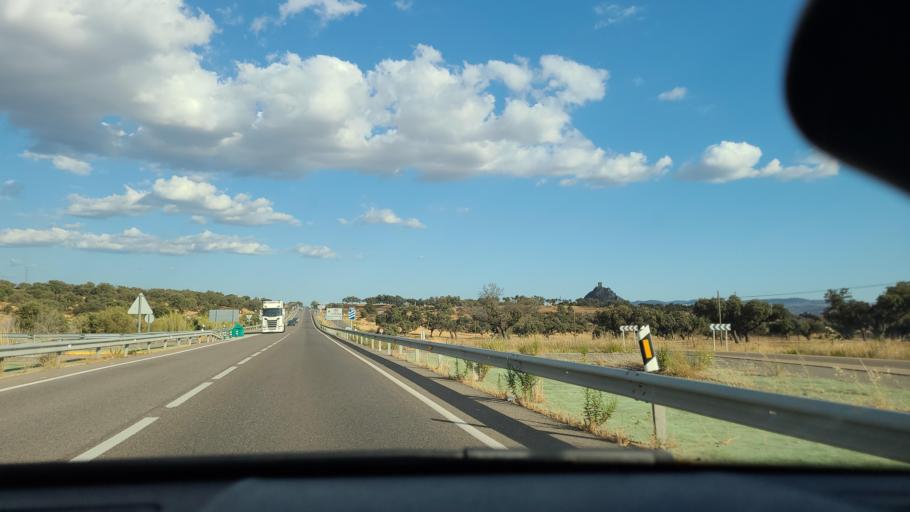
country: ES
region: Andalusia
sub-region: Province of Cordoba
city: Belmez
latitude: 38.2906
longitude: -5.2268
